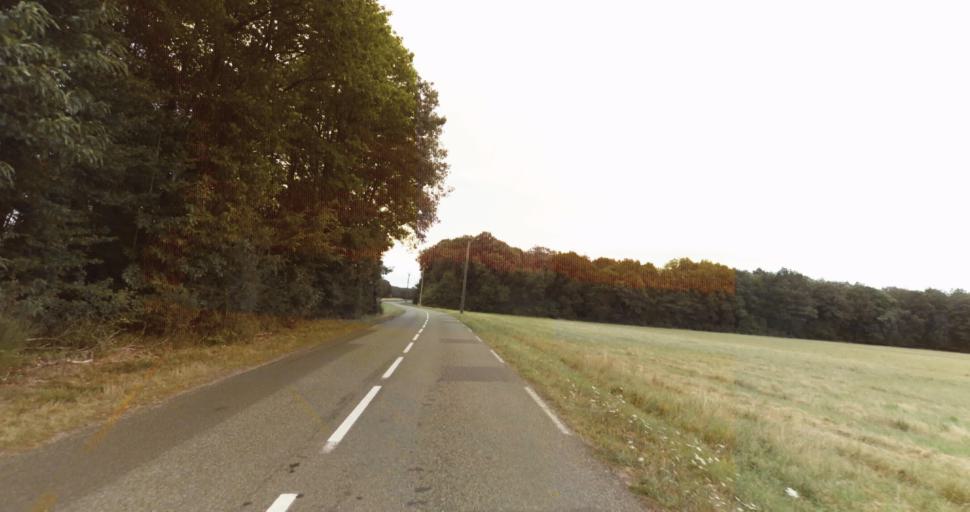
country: FR
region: Haute-Normandie
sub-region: Departement de l'Eure
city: Gravigny
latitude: 48.9841
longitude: 1.2598
